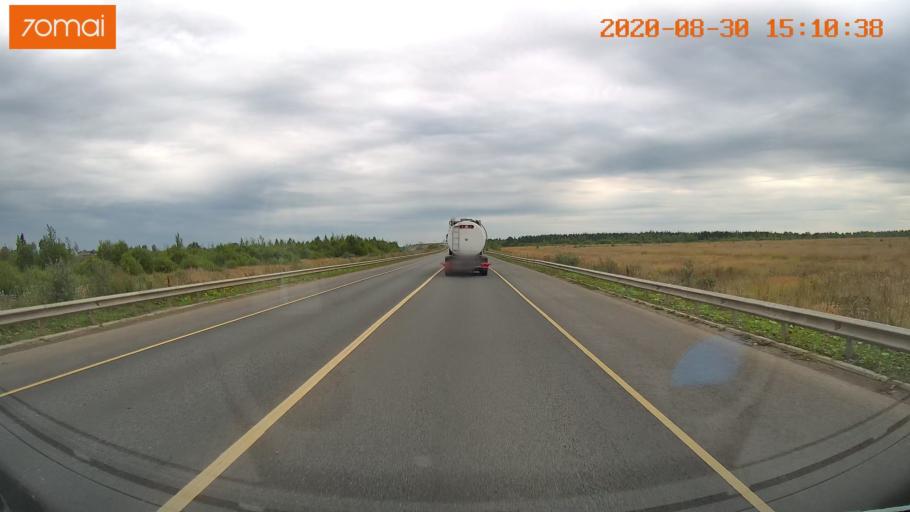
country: RU
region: Ivanovo
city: Staraya Vichuga
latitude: 57.2154
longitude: 41.8642
